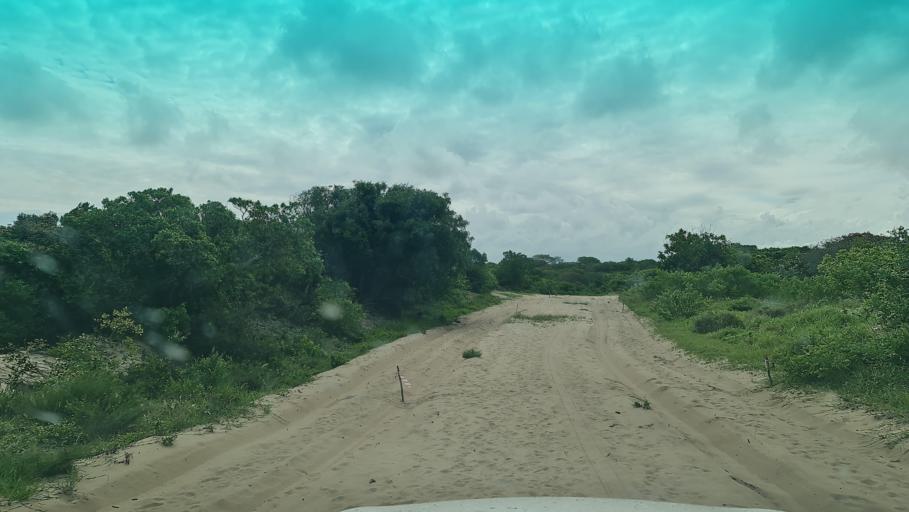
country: MZ
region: Maputo
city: Manhica
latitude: -25.4415
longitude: 32.9333
